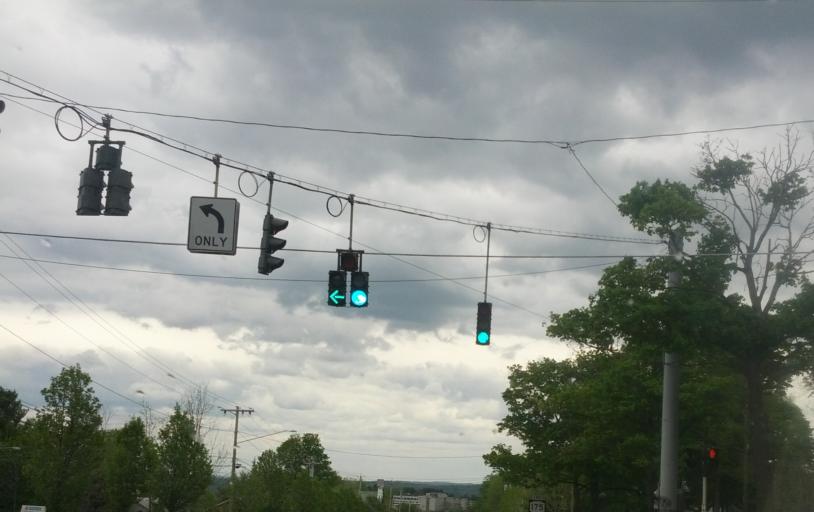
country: US
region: New York
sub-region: Onondaga County
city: Nedrow
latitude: 43.0049
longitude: -76.1837
